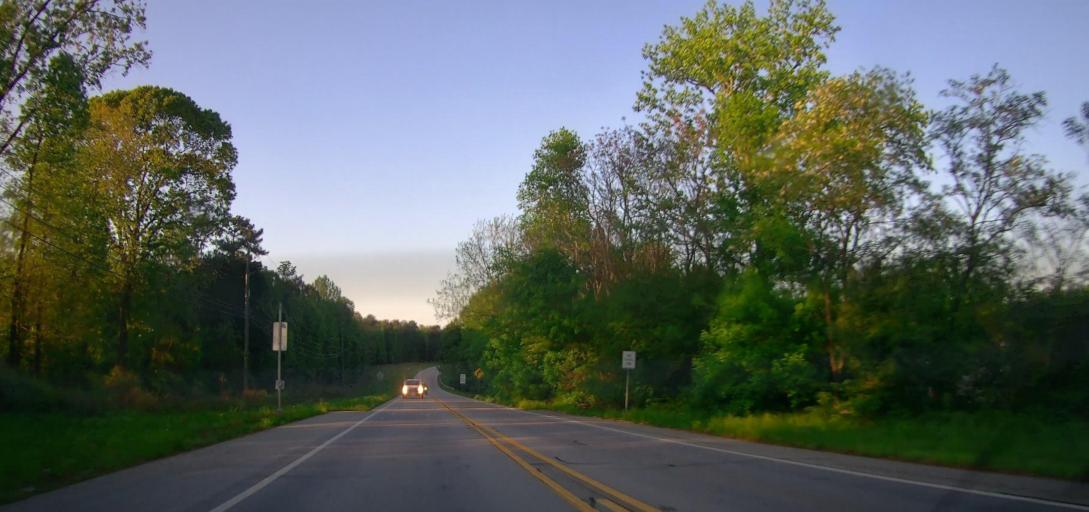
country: US
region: Georgia
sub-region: Newton County
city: Oakwood
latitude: 33.5420
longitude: -83.9492
